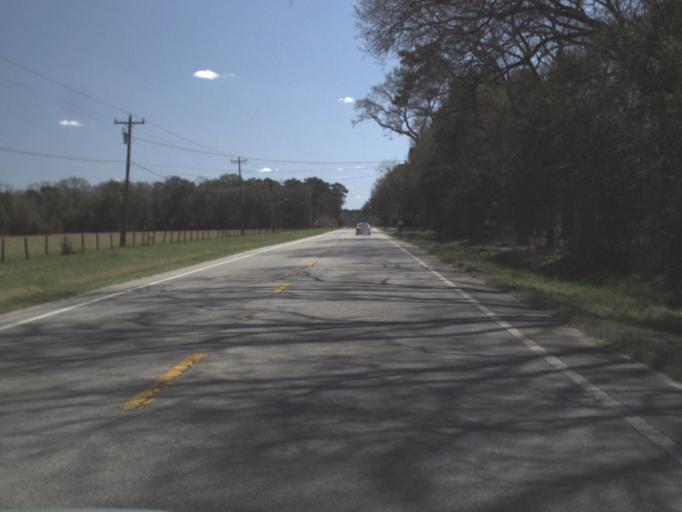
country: US
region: Florida
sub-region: Gadsden County
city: Gretna
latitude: 30.6700
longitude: -84.6137
